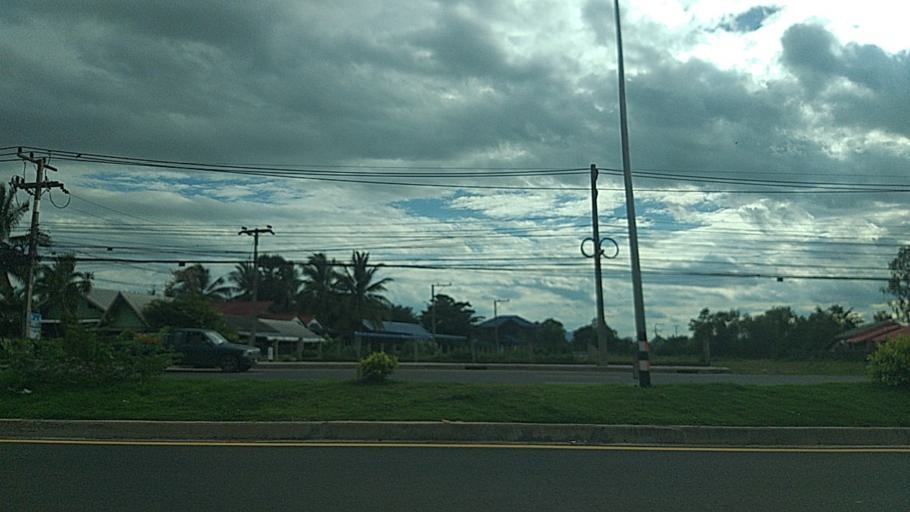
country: TH
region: Surin
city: Prasat
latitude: 14.6240
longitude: 103.4111
